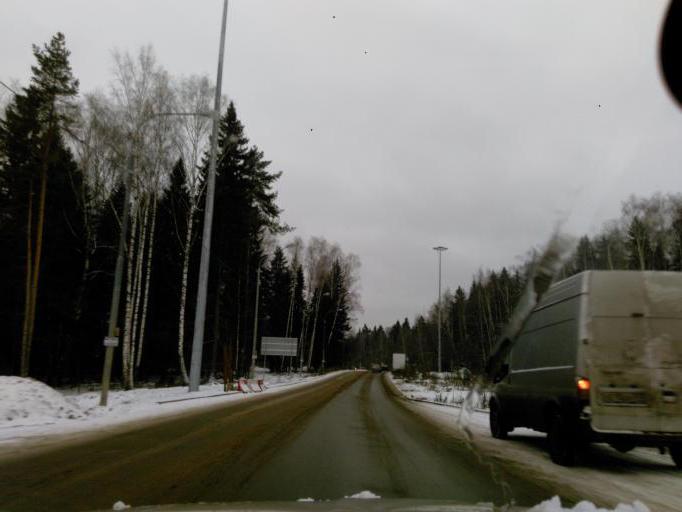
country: RU
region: Moskovskaya
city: Mendeleyevo
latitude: 56.0163
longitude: 37.2065
